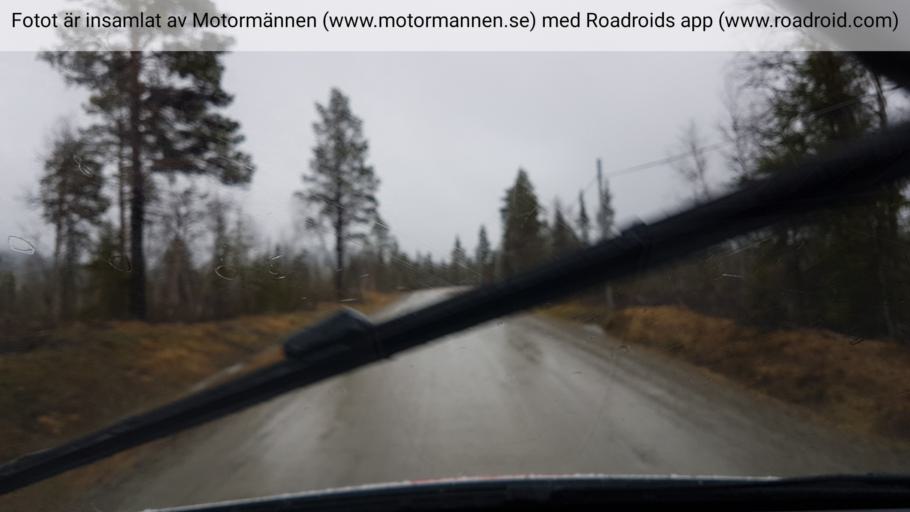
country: SE
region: Jaemtland
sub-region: Are Kommun
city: Jarpen
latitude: 62.6157
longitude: 13.1961
